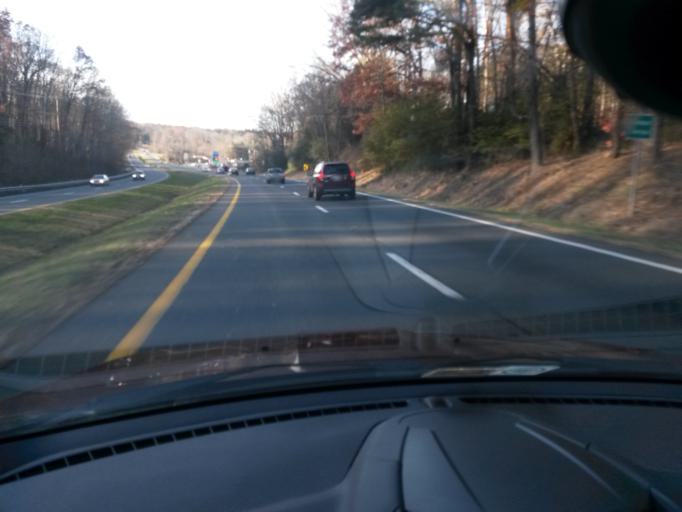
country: US
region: Virginia
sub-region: Campbell County
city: Concord
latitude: 37.3688
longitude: -79.0146
